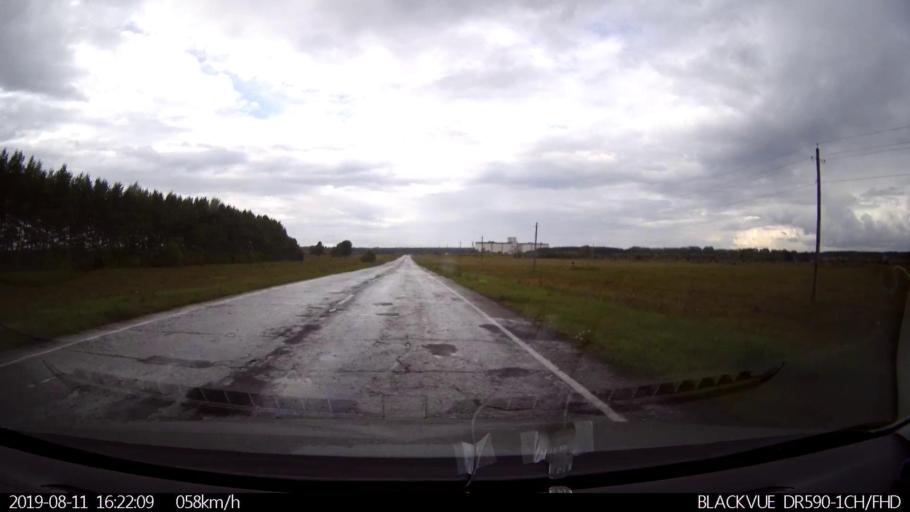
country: RU
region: Ulyanovsk
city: Mayna
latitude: 54.0856
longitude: 47.5944
